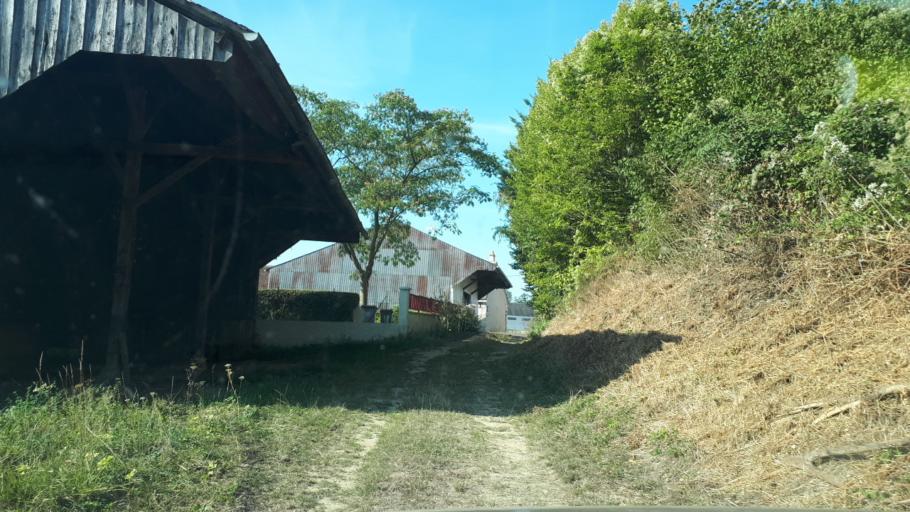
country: FR
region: Centre
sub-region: Departement du Loir-et-Cher
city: Villiers-sur-Loir
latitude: 47.8275
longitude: 0.9721
